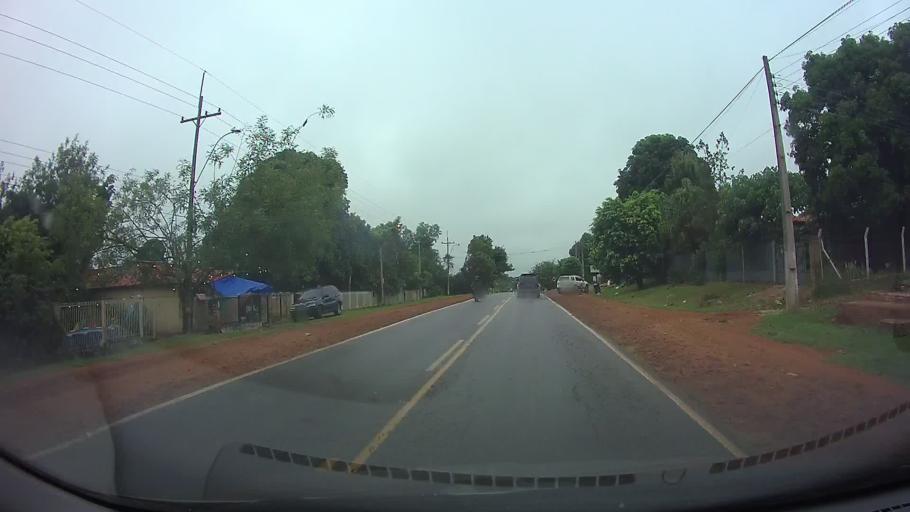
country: PY
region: Central
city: Ita
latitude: -25.4331
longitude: -57.3663
